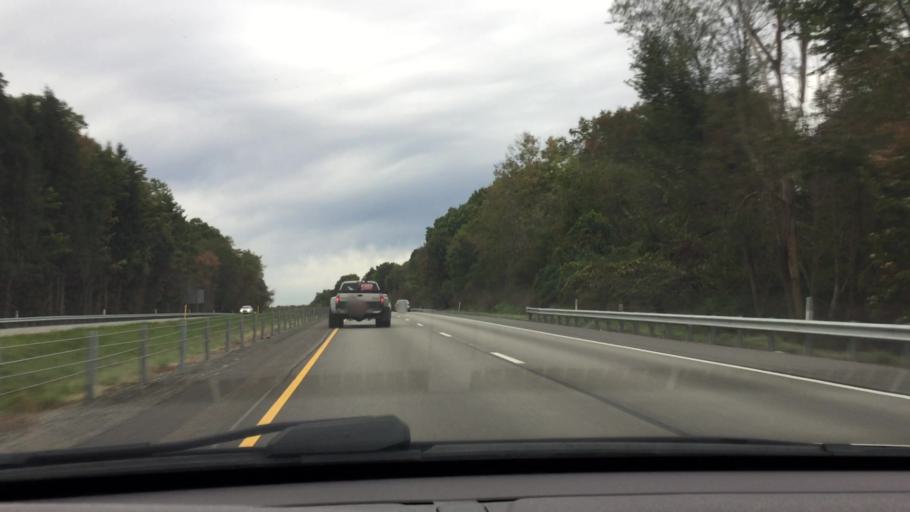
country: US
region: Pennsylvania
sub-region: Beaver County
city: Ambridge
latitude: 40.5648
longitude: -80.2803
